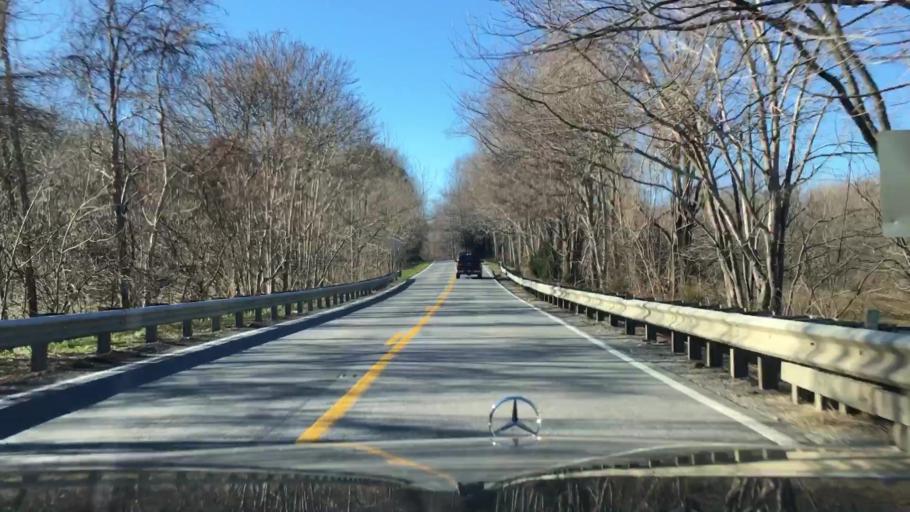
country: US
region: Virginia
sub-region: Botetourt County
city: Blue Ridge
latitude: 37.2611
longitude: -79.7480
